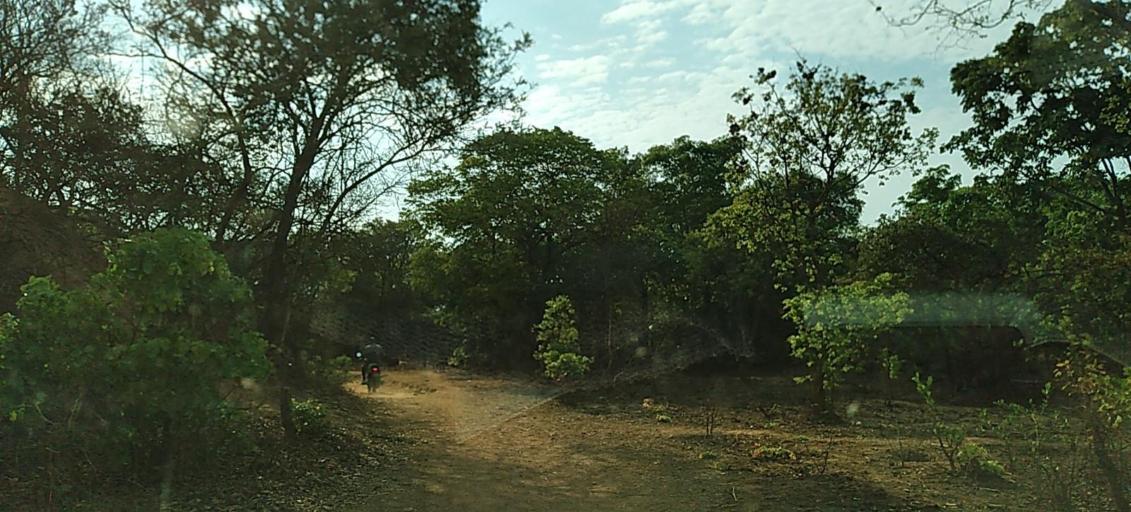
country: ZM
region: Copperbelt
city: Kalulushi
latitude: -12.9640
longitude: 27.7017
